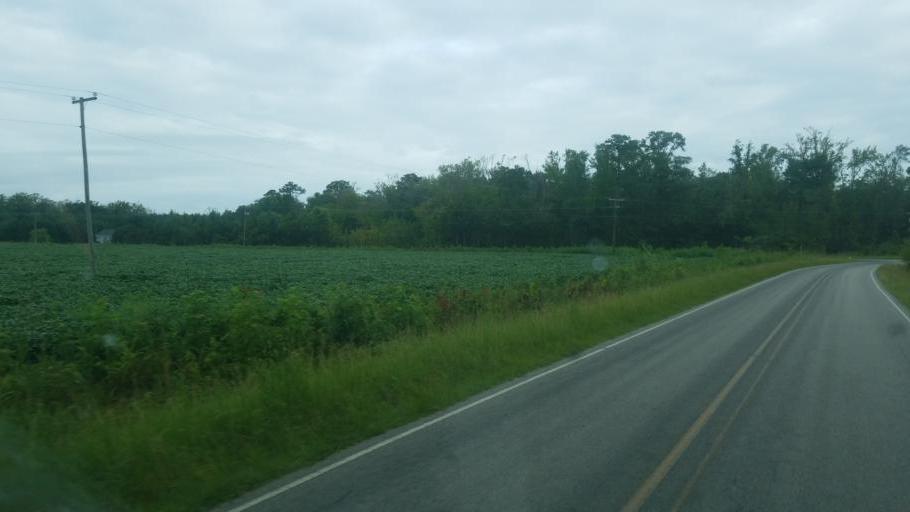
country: US
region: North Carolina
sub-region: Tyrrell County
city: Columbia
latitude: 35.9462
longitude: -76.2815
